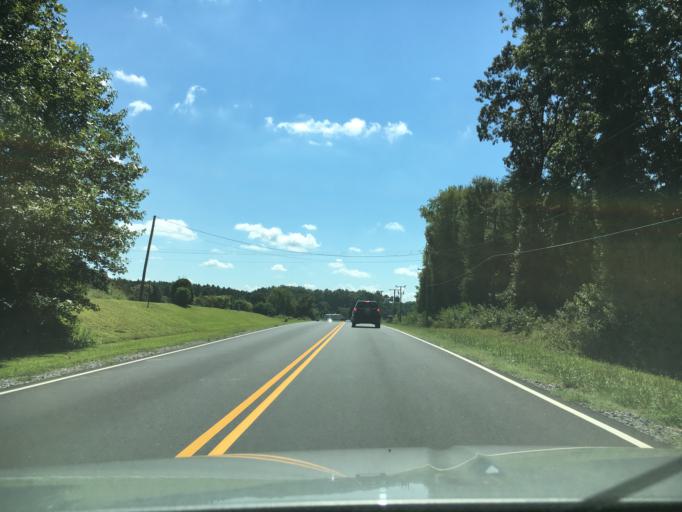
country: US
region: Virginia
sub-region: Amelia County
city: Amelia Court House
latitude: 37.3717
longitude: -77.9059
